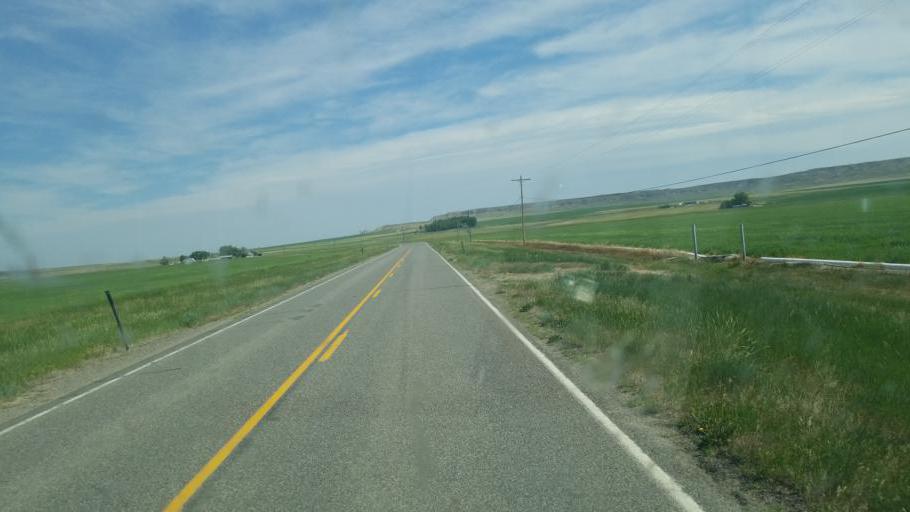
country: US
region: Wyoming
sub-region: Park County
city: Powell
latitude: 44.7567
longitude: -108.9323
